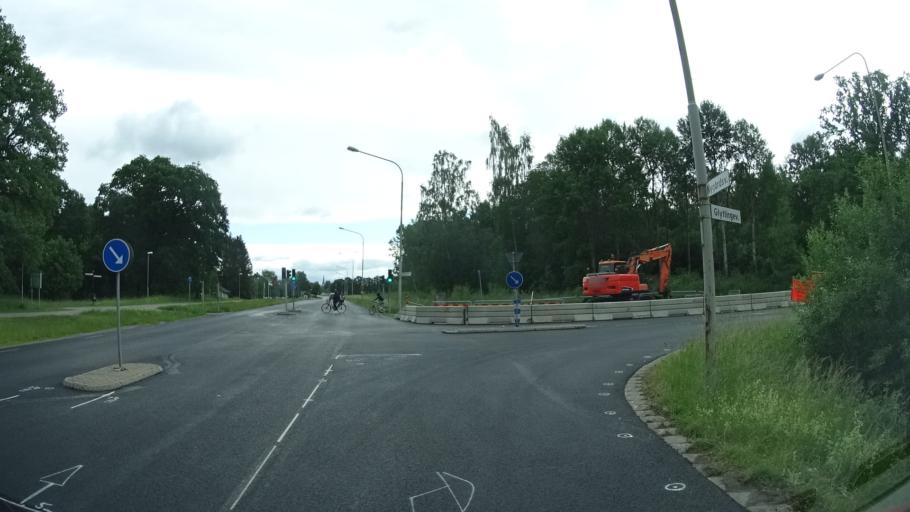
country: SE
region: OEstergoetland
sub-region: Linkopings Kommun
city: Linkoping
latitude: 58.4236
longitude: 15.5710
